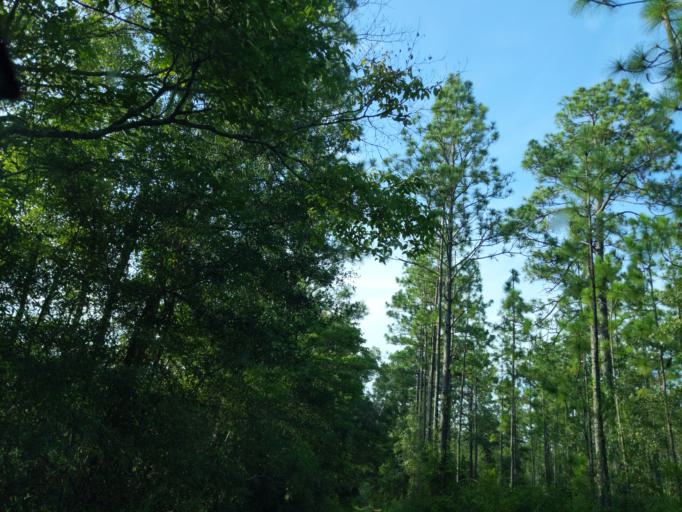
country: US
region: Florida
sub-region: Leon County
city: Tallahassee
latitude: 30.3573
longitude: -84.3611
